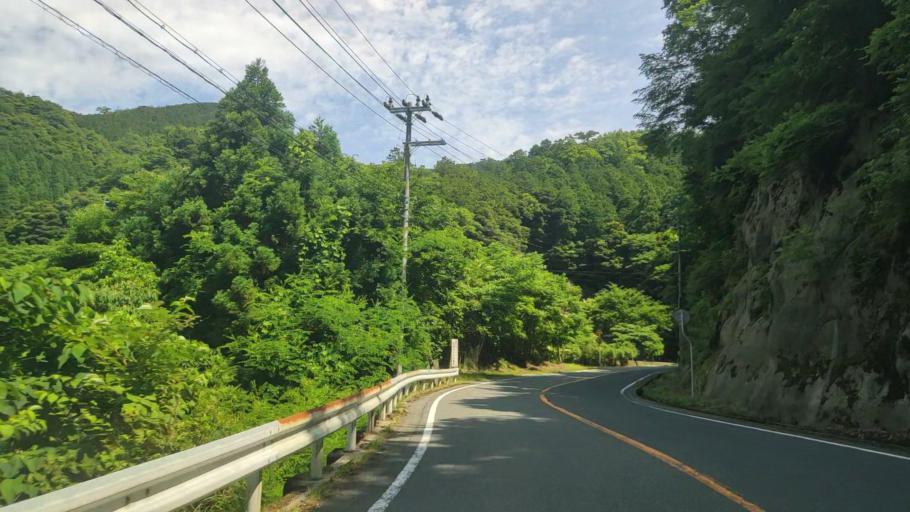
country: JP
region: Hyogo
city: Toyooka
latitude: 35.6353
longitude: 134.7806
